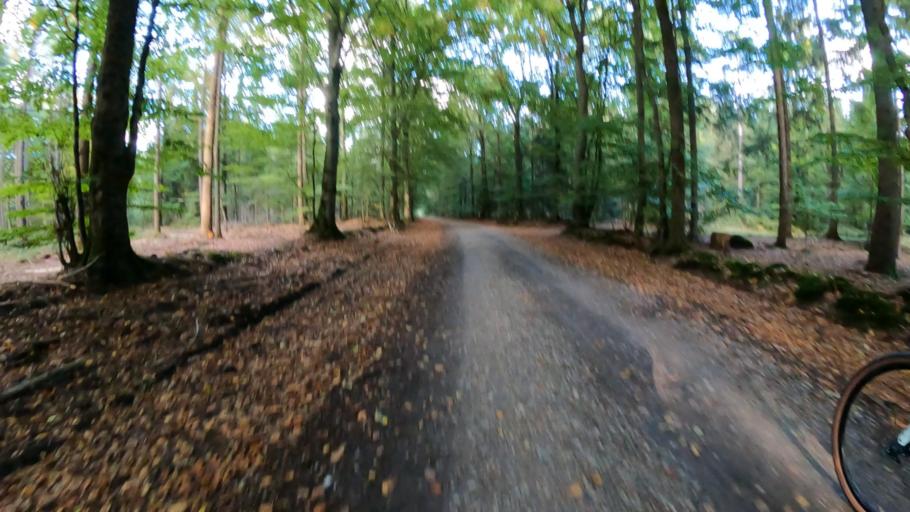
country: DE
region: Schleswig-Holstein
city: Hartenholm
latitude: 53.9082
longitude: 10.0725
